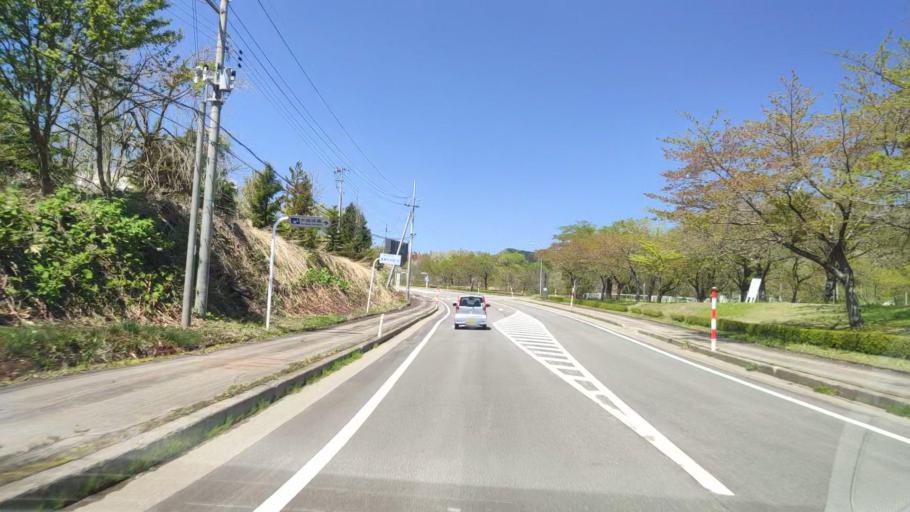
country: JP
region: Akita
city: Omagari
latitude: 39.4331
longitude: 140.4411
